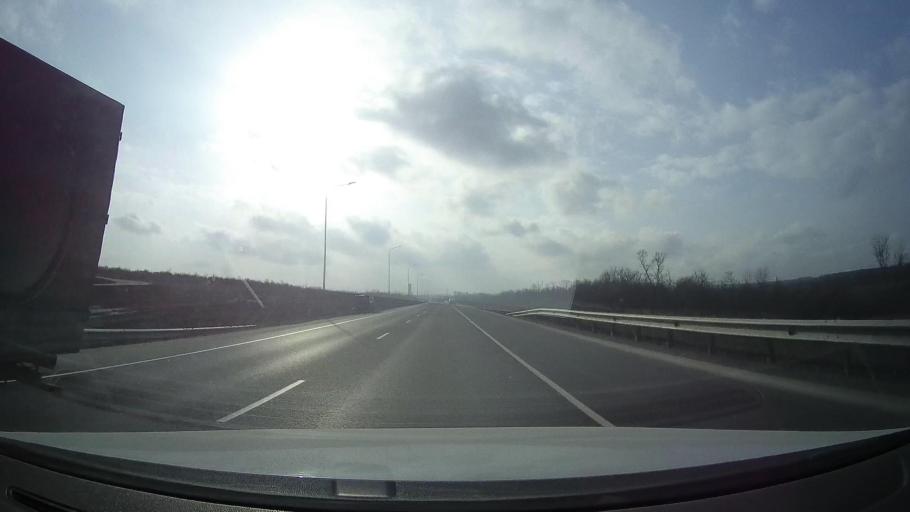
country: RU
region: Rostov
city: Grushevskaya
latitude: 47.4252
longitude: 39.8648
